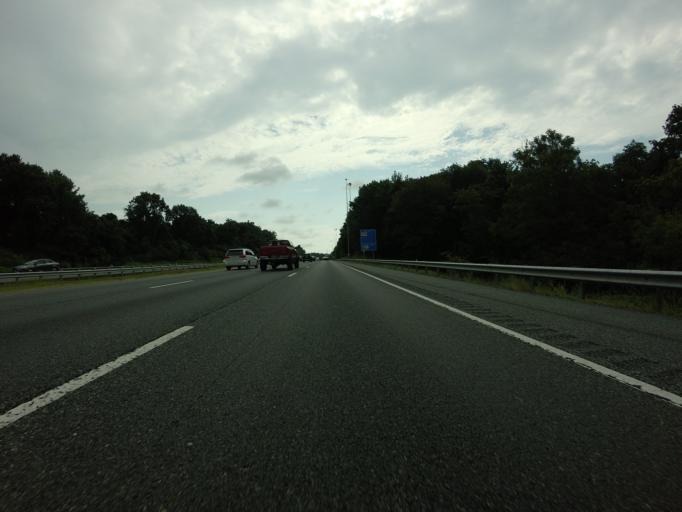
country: US
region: Maryland
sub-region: Cecil County
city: Perryville
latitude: 39.5855
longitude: -76.0897
